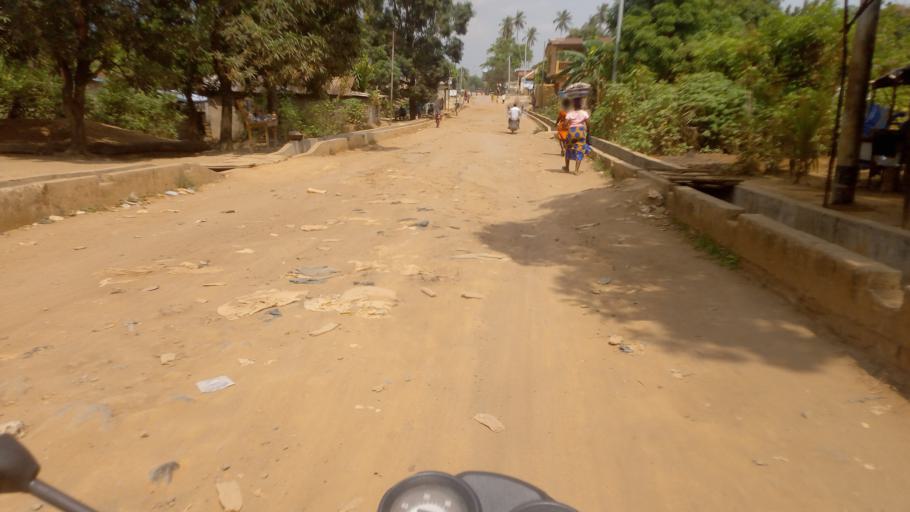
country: SL
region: Western Area
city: Waterloo
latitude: 8.3225
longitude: -13.0640
